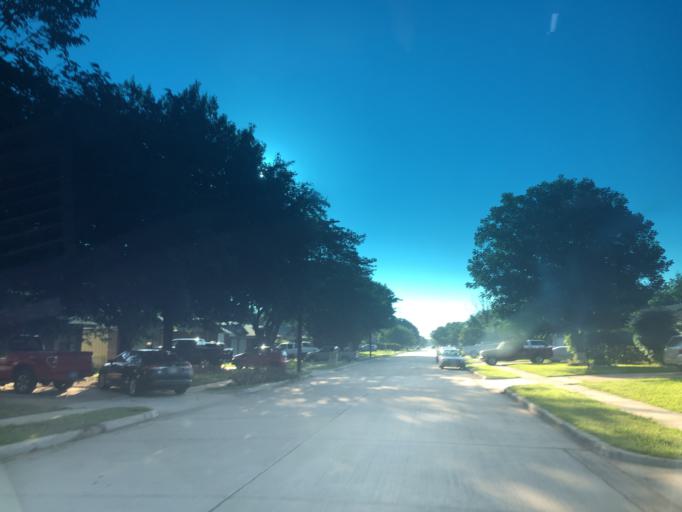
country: US
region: Texas
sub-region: Dallas County
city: Grand Prairie
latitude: 32.7034
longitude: -97.0142
